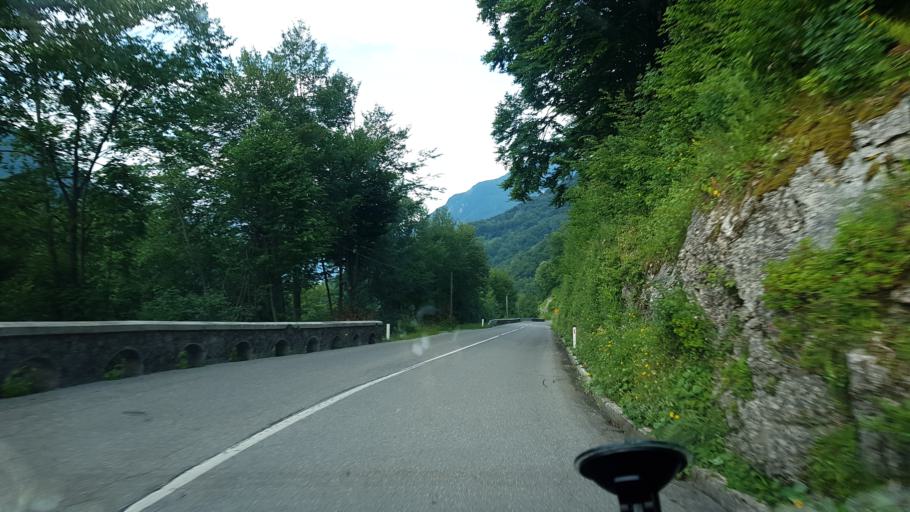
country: SI
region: Bovec
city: Bovec
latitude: 46.3023
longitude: 13.4480
